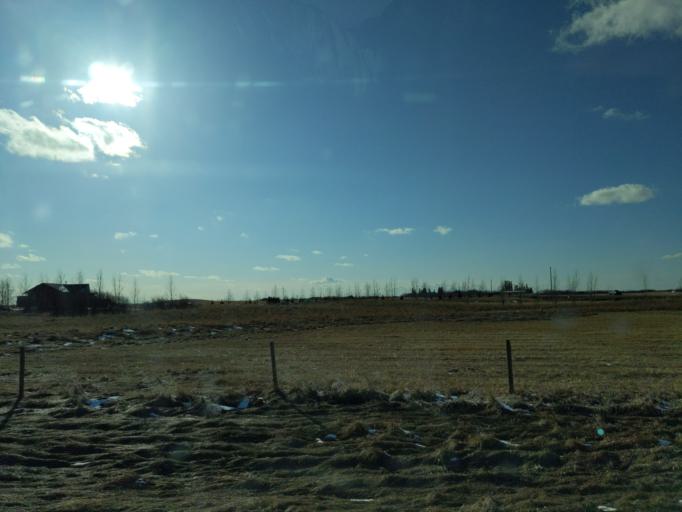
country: CA
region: Saskatchewan
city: Lloydminster
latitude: 53.3357
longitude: -109.8815
